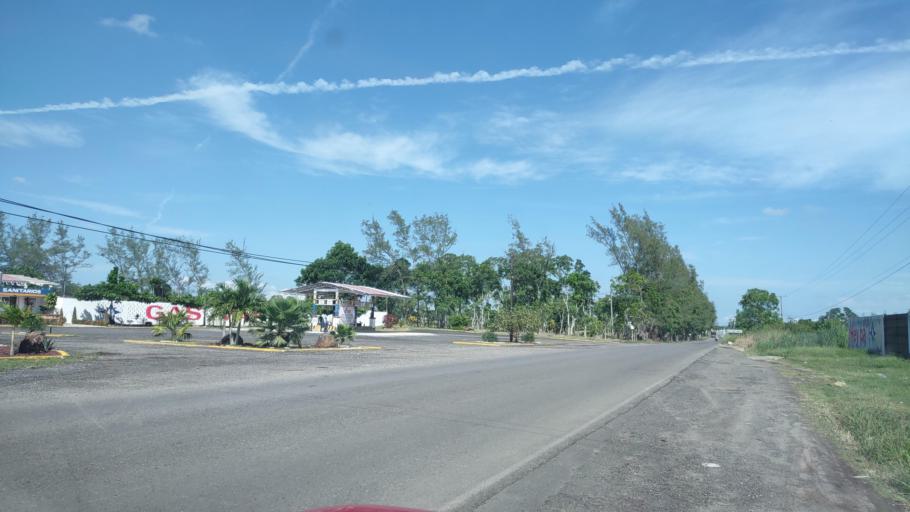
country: MX
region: Veracruz
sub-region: Martinez de la Torre
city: La Union Paso Largo
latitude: 20.1369
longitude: -96.9979
